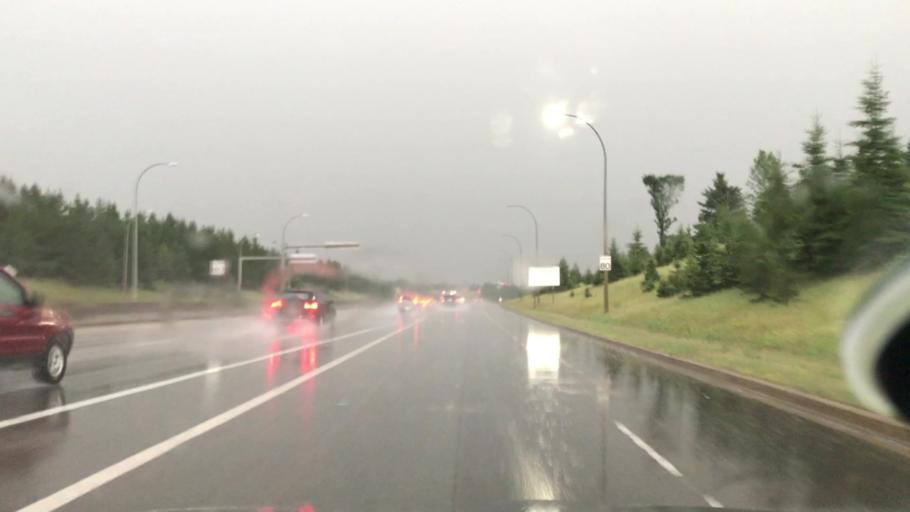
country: CA
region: Alberta
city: Edmonton
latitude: 53.4824
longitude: -113.5660
